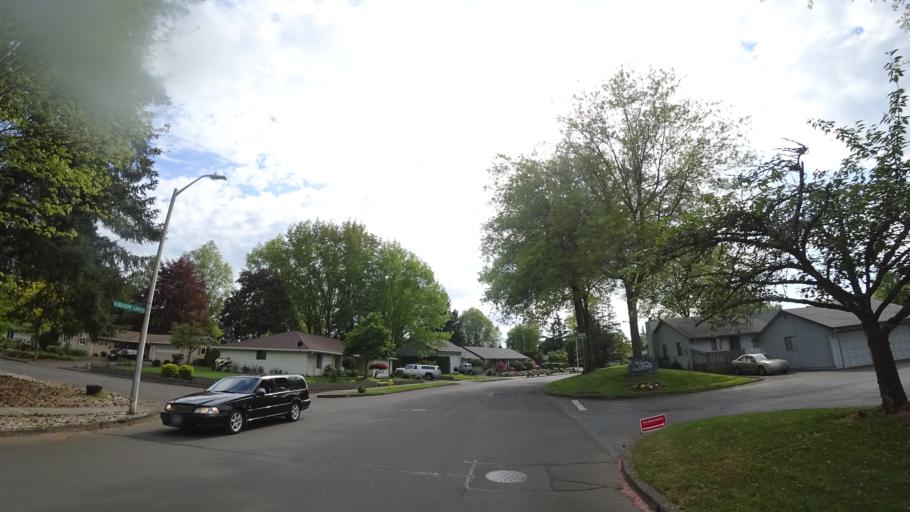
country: US
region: Oregon
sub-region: Washington County
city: Hillsboro
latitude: 45.5009
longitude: -122.9620
